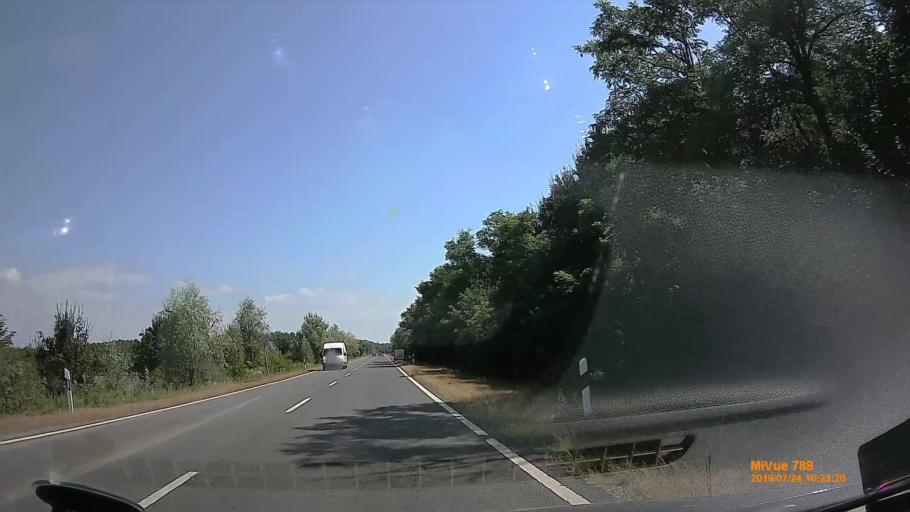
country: HU
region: Szabolcs-Szatmar-Bereg
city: Vasarosnameny
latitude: 48.1473
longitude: 22.3658
